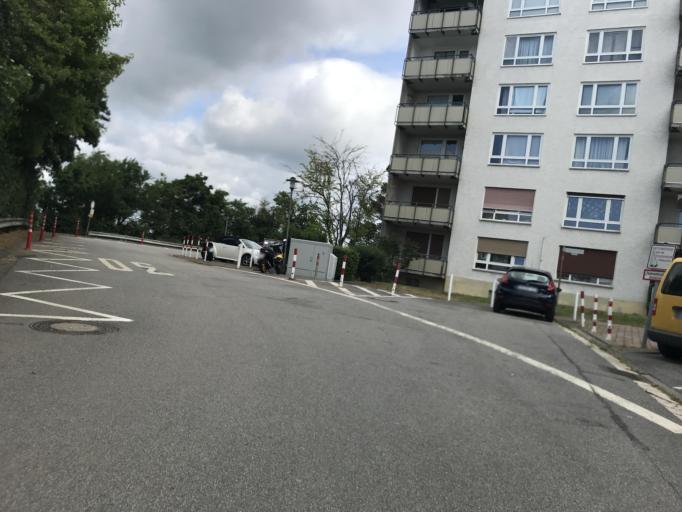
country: DE
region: Rheinland-Pfalz
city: Sorgenloch
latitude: 49.8923
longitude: 8.2084
